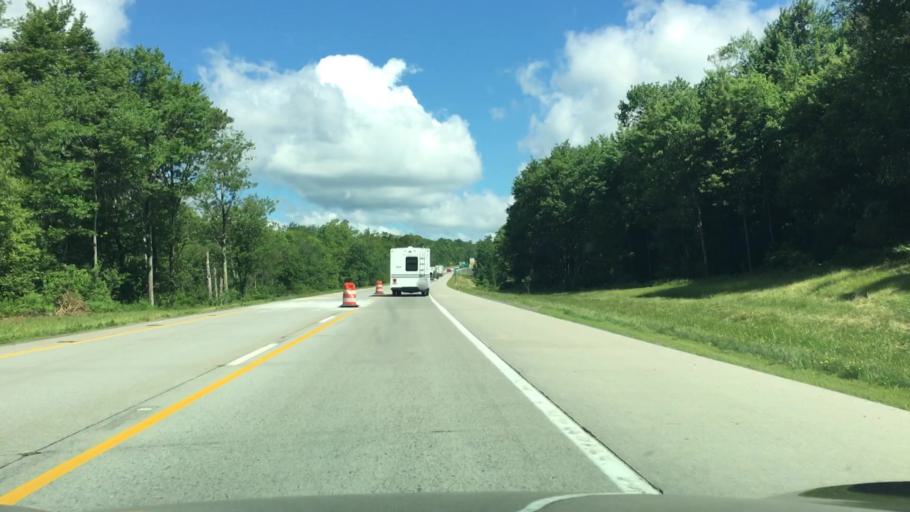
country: US
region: Pennsylvania
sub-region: Lackawanna County
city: Moscow
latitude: 41.2407
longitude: -75.5115
